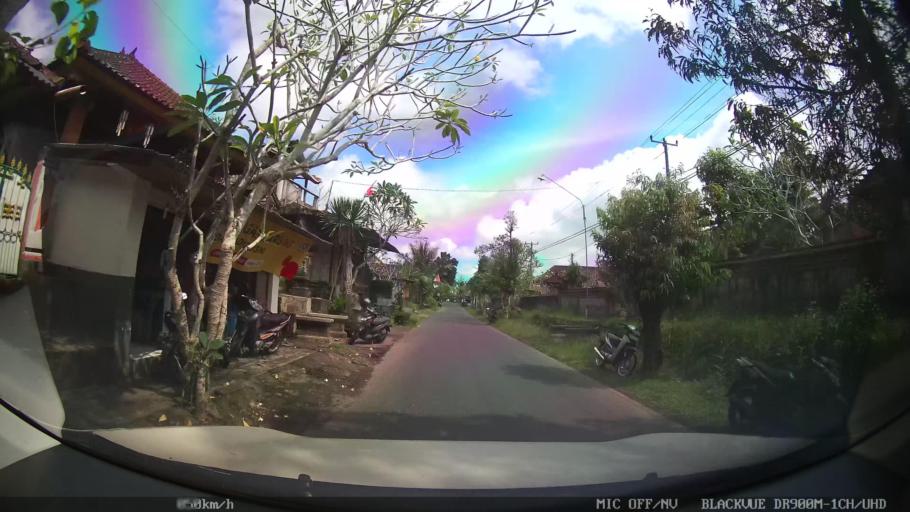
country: ID
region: Bali
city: Banjar Mulung
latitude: -8.4965
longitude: 115.3205
